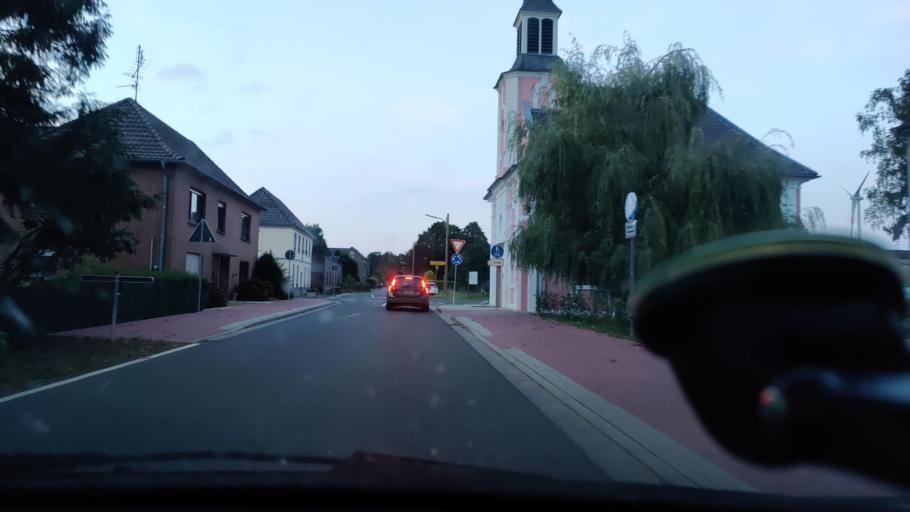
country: DE
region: North Rhine-Westphalia
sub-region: Regierungsbezirk Dusseldorf
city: Goch
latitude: 51.7220
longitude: 6.1919
